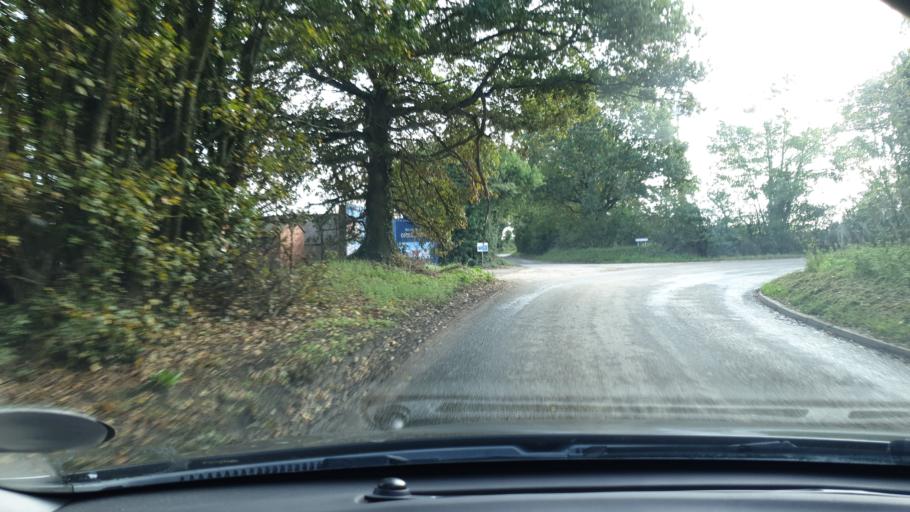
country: GB
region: England
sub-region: Essex
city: Manningtree
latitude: 51.9343
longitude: 1.0471
